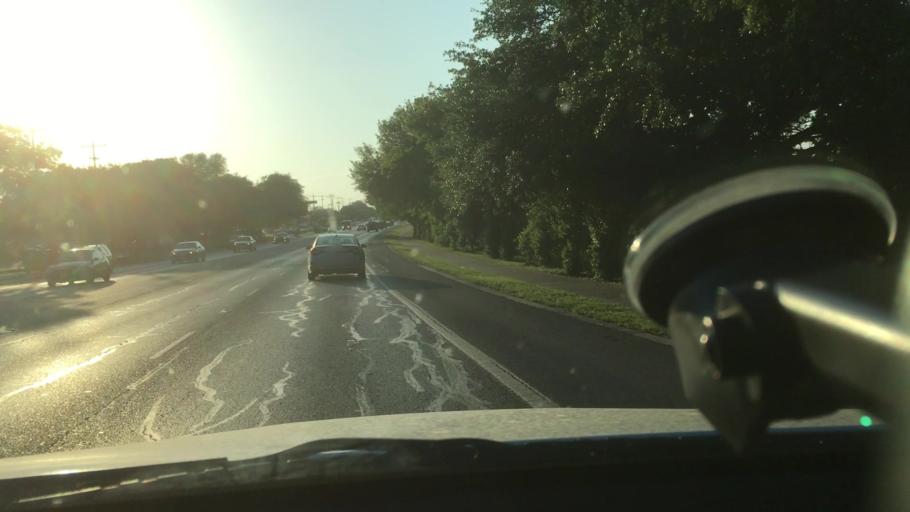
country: US
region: Texas
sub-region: Bexar County
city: Universal City
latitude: 29.5543
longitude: -98.3119
